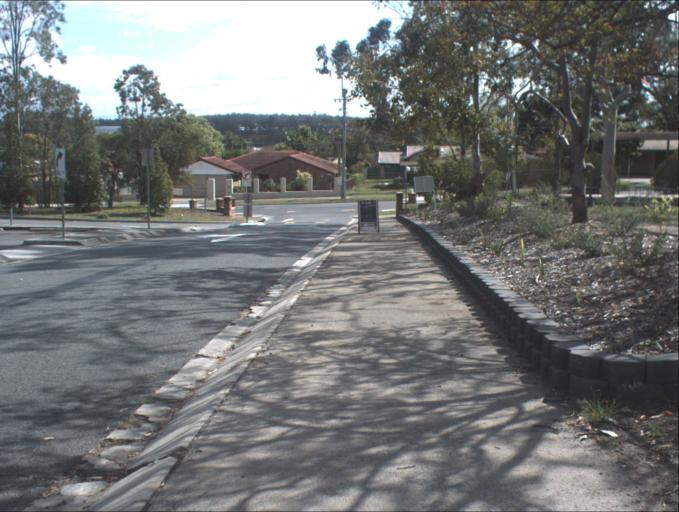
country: AU
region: Queensland
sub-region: Logan
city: Park Ridge South
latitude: -27.6702
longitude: 153.0348
